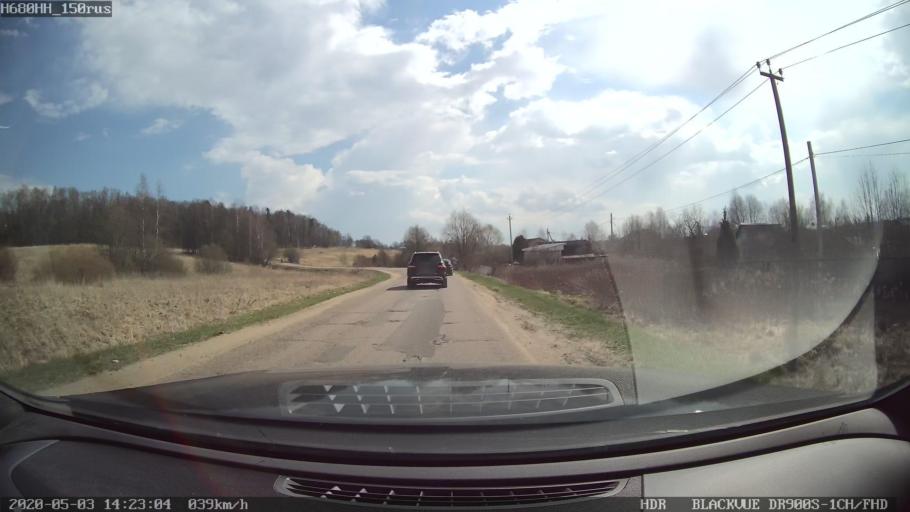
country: RU
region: Moskovskaya
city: Solnechnogorsk
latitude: 56.2552
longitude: 36.9918
